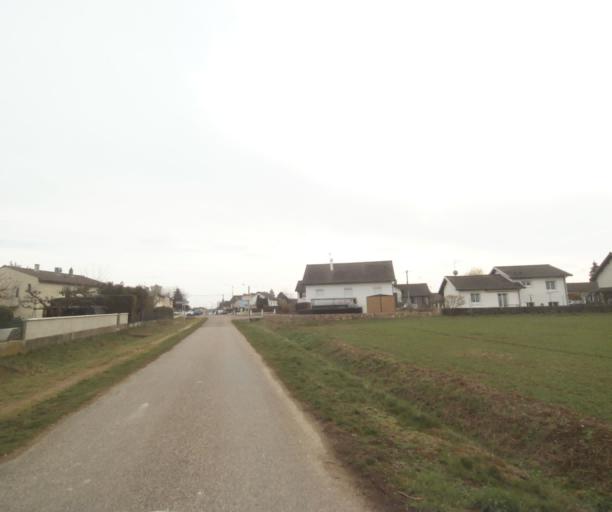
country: FR
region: Champagne-Ardenne
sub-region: Departement de la Haute-Marne
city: Villiers-en-Lieu
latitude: 48.6692
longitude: 4.8922
